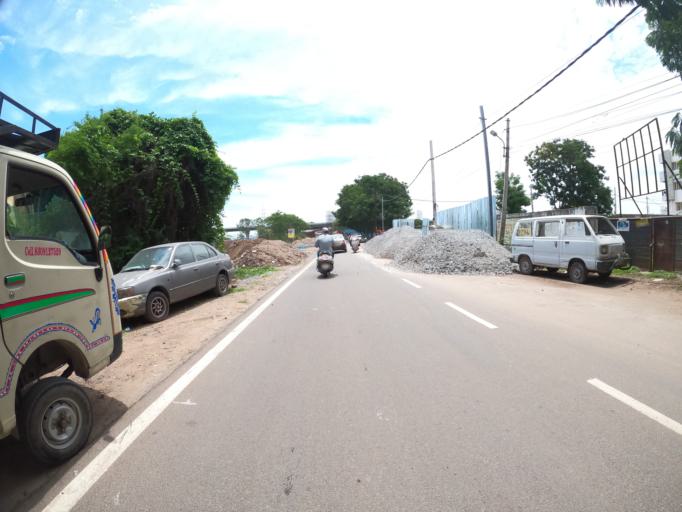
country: IN
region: Telangana
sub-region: Hyderabad
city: Hyderabad
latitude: 17.3715
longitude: 78.4269
